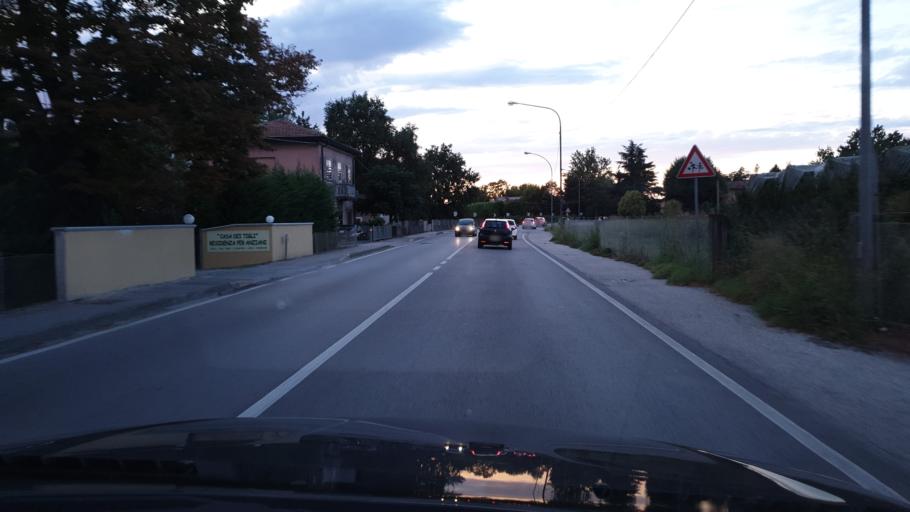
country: IT
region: Emilia-Romagna
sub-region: Provincia di Ravenna
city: Glorie
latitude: 44.4779
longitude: 12.0710
